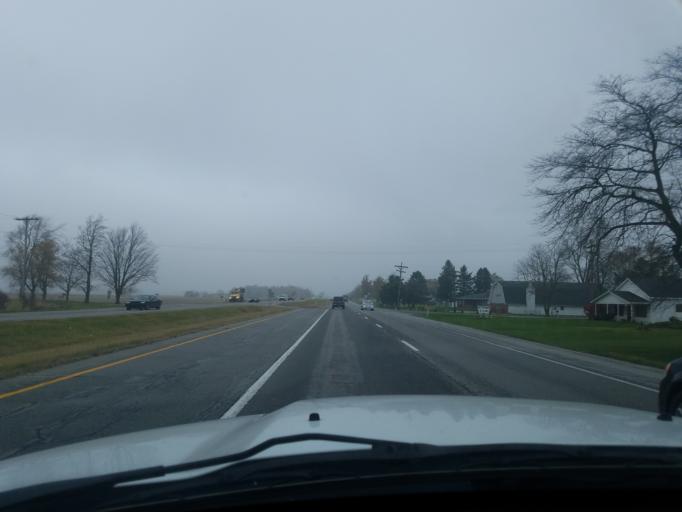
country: US
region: Indiana
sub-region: Howard County
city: Indian Heights
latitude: 40.3458
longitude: -86.1270
